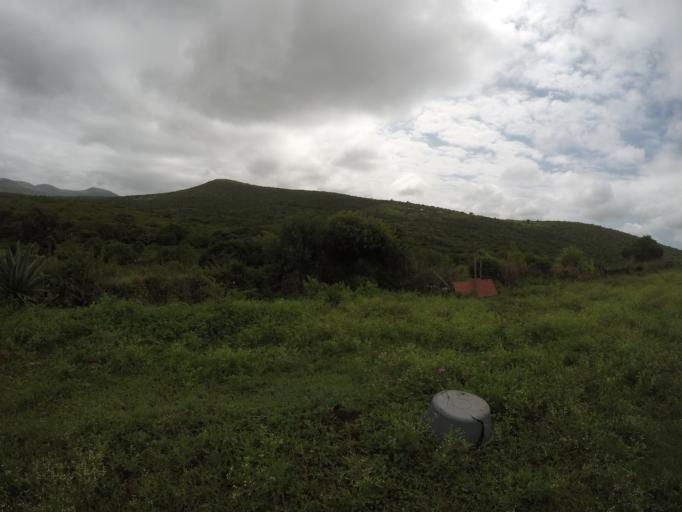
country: ZA
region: KwaZulu-Natal
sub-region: uThungulu District Municipality
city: Empangeni
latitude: -28.6273
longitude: 31.8809
